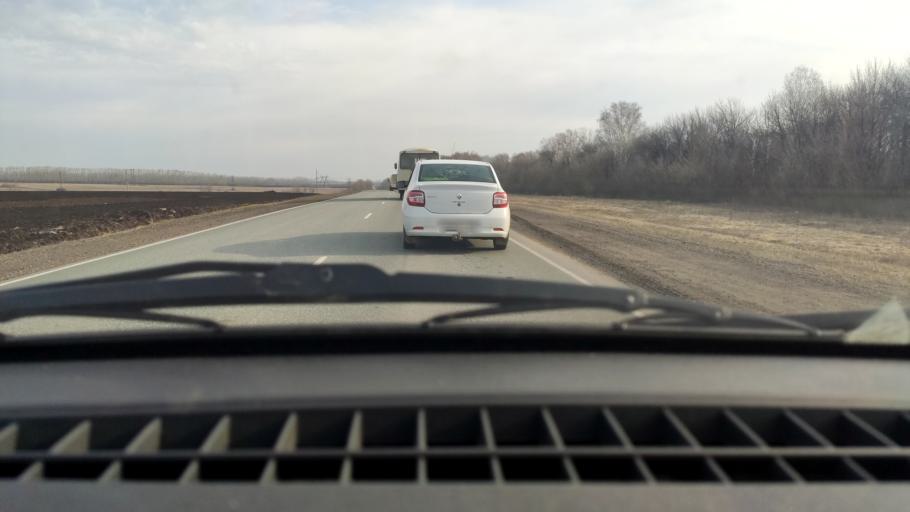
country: RU
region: Bashkortostan
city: Chishmy
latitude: 54.5043
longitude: 55.2878
